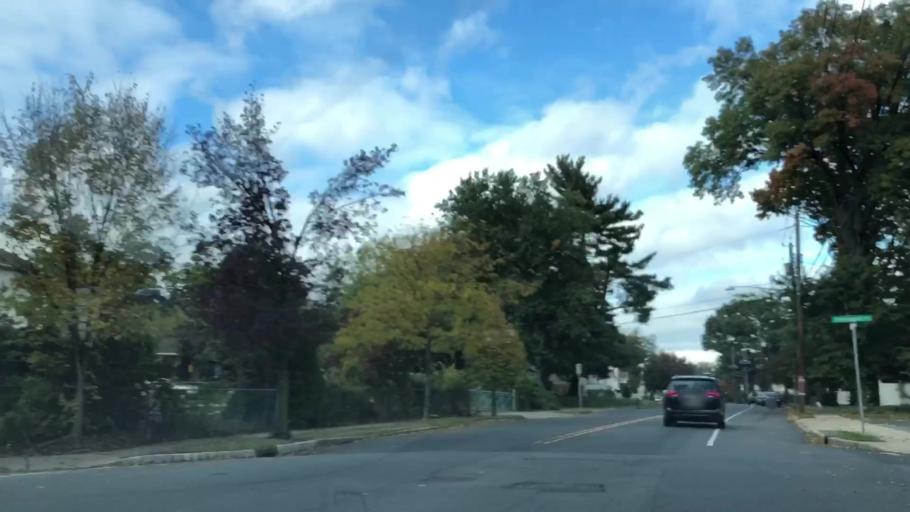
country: US
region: New Jersey
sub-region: Essex County
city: Glen Ridge
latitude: 40.7916
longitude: -74.2192
